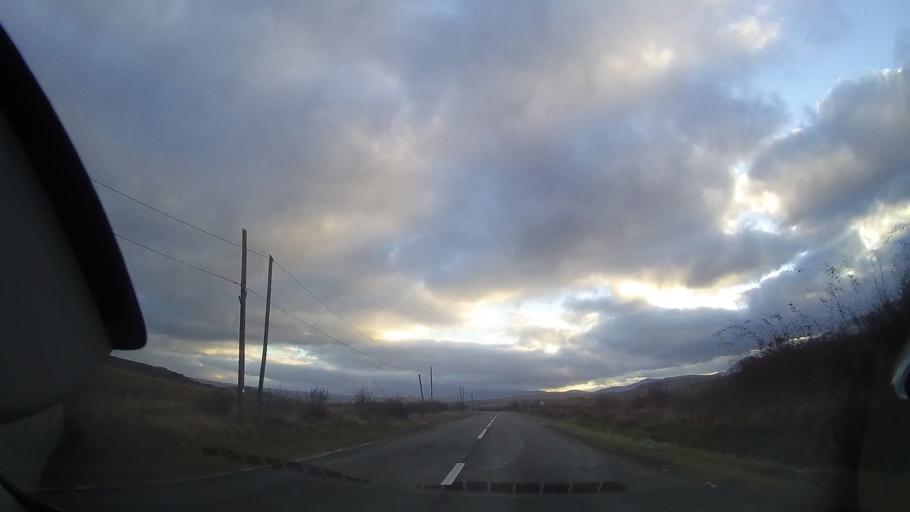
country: RO
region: Cluj
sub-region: Comuna Sancraiu
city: Sancraiu
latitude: 46.8161
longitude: 22.9943
